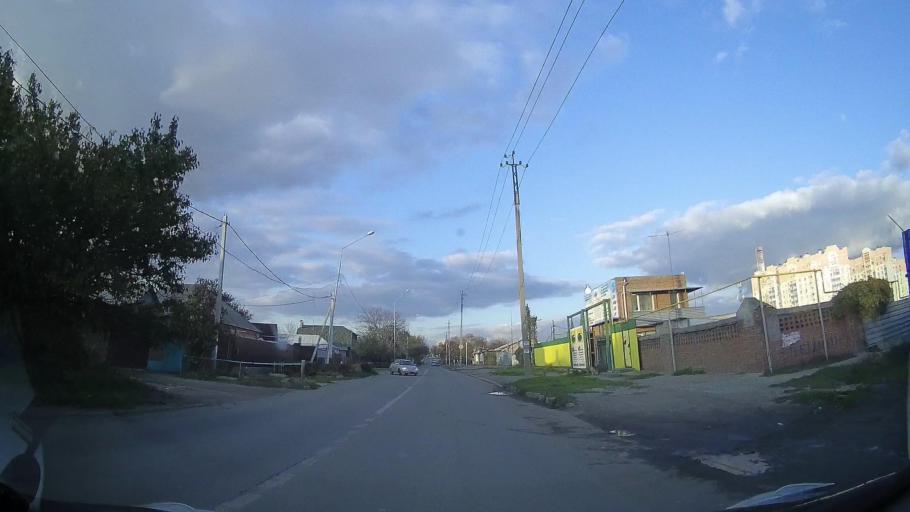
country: RU
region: Rostov
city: Imeni Chkalova
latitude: 47.2410
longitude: 39.7771
